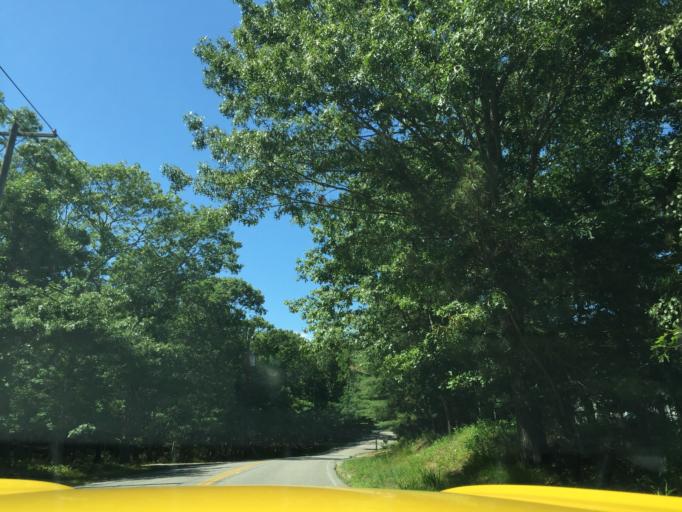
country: US
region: New York
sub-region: Suffolk County
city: Springs
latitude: 41.0059
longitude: -72.1398
